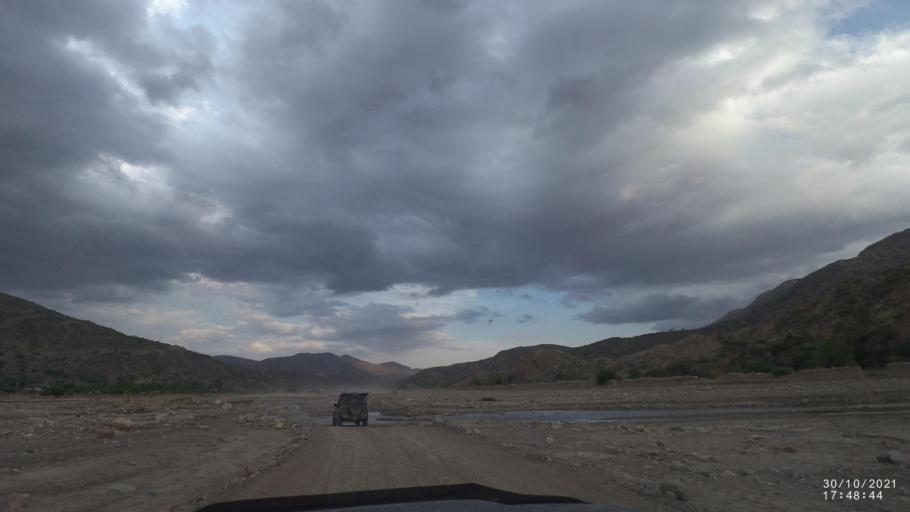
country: BO
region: Cochabamba
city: Sipe Sipe
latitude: -17.5353
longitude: -66.5177
